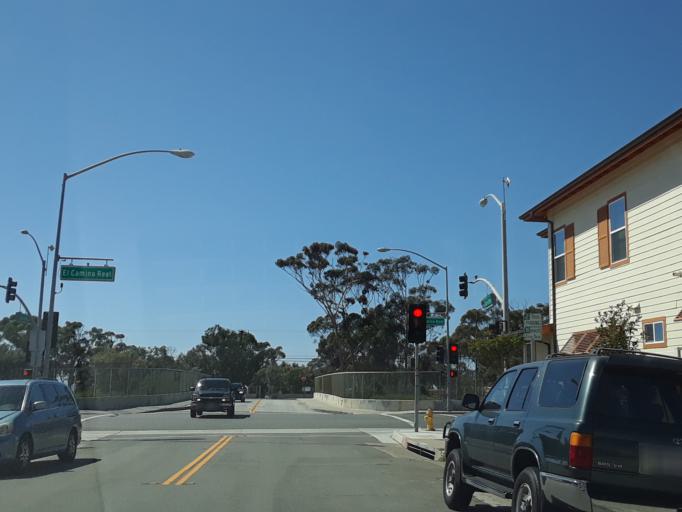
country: US
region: California
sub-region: Orange County
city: San Clemente
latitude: 33.4054
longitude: -117.5973
